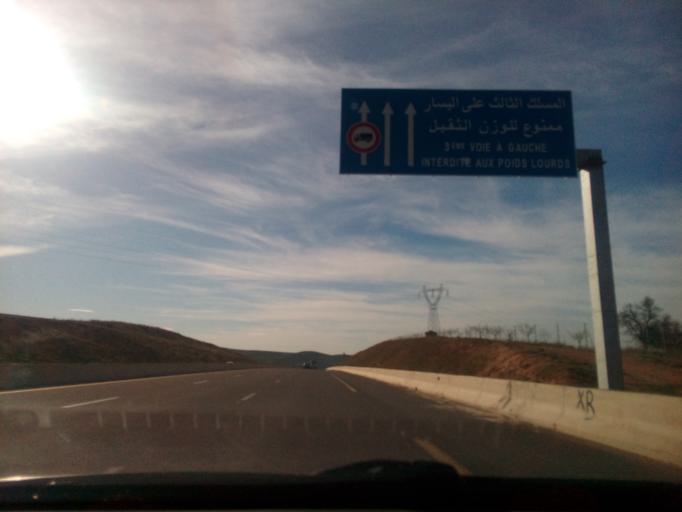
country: DZ
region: Tlemcen
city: Hennaya
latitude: 34.9154
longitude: -1.3895
